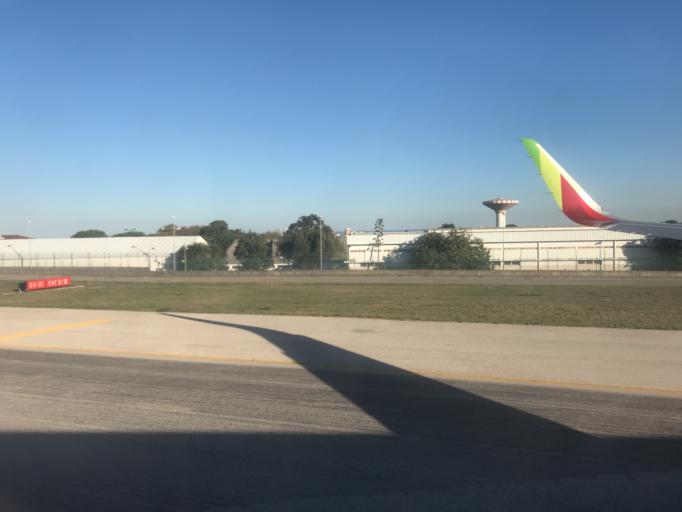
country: PT
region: Lisbon
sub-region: Loures
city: Camarate
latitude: 38.7834
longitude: -9.1325
